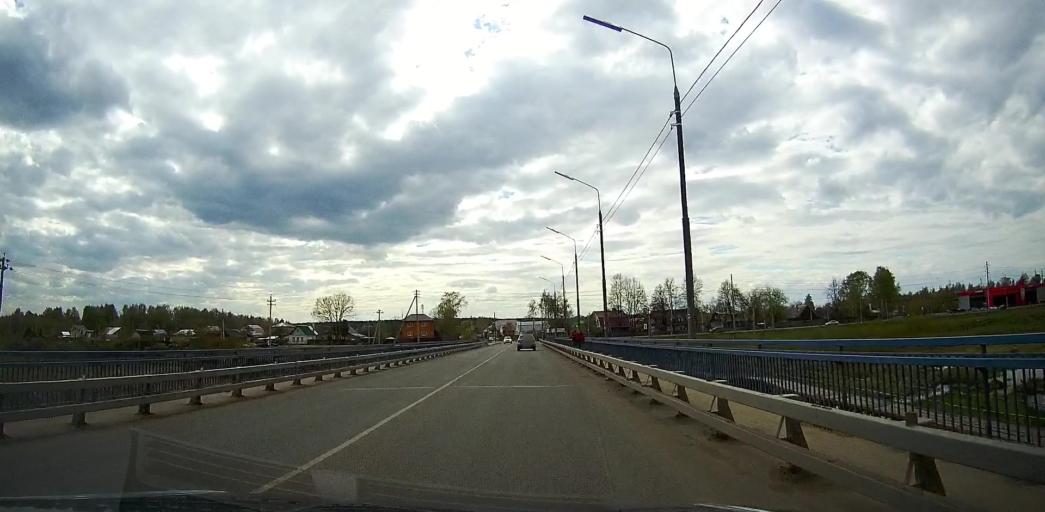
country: RU
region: Moskovskaya
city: Pavlovskiy Posad
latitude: 55.7697
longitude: 38.6467
